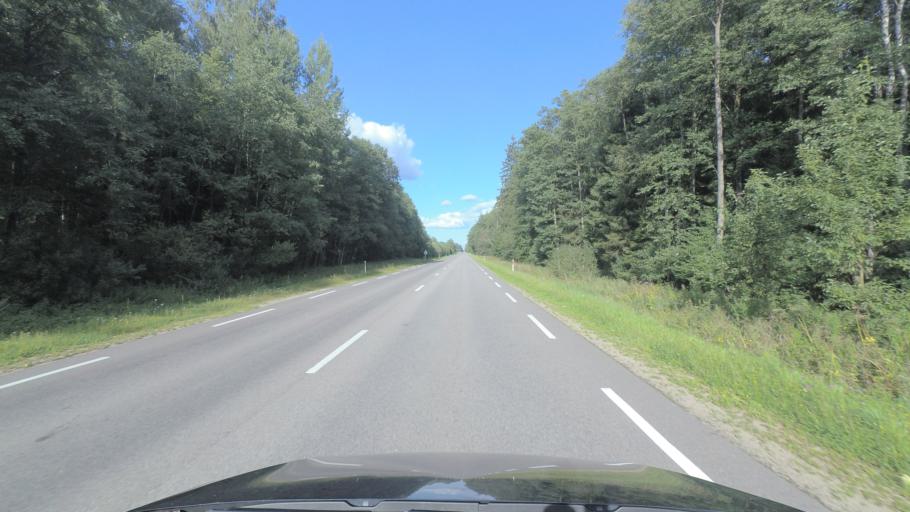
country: LT
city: Pabrade
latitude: 54.9584
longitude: 25.6877
